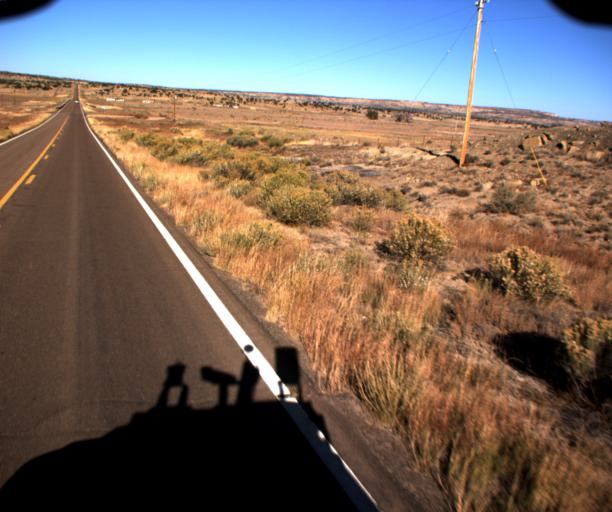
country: US
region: Arizona
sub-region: Apache County
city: Ganado
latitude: 35.7480
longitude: -109.8723
